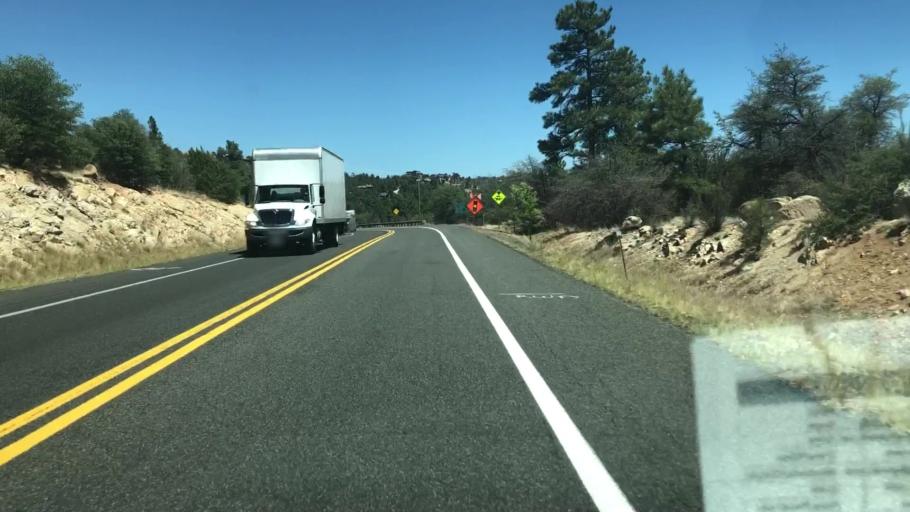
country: US
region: Arizona
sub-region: Yavapai County
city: Prescott
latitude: 34.5781
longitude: -112.5224
